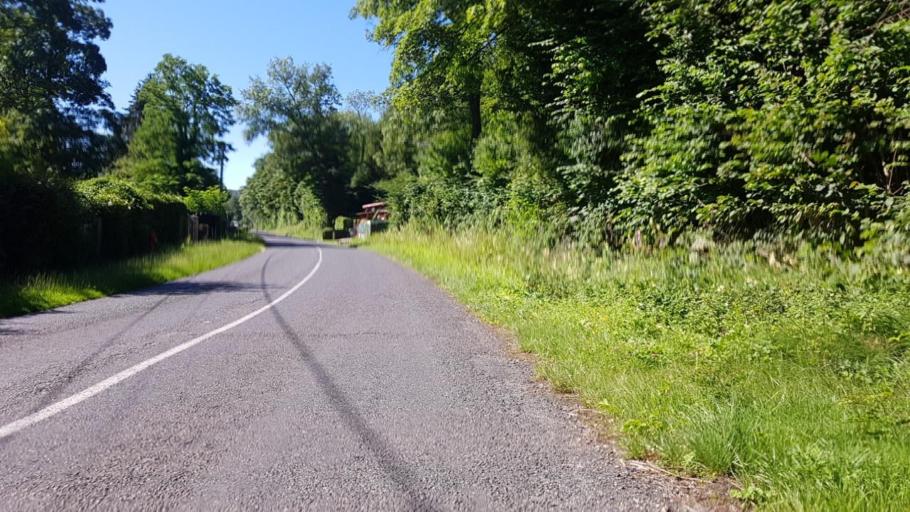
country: FR
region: Picardie
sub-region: Departement de l'Aisne
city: Chezy-sur-Marne
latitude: 48.9971
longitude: 3.3419
